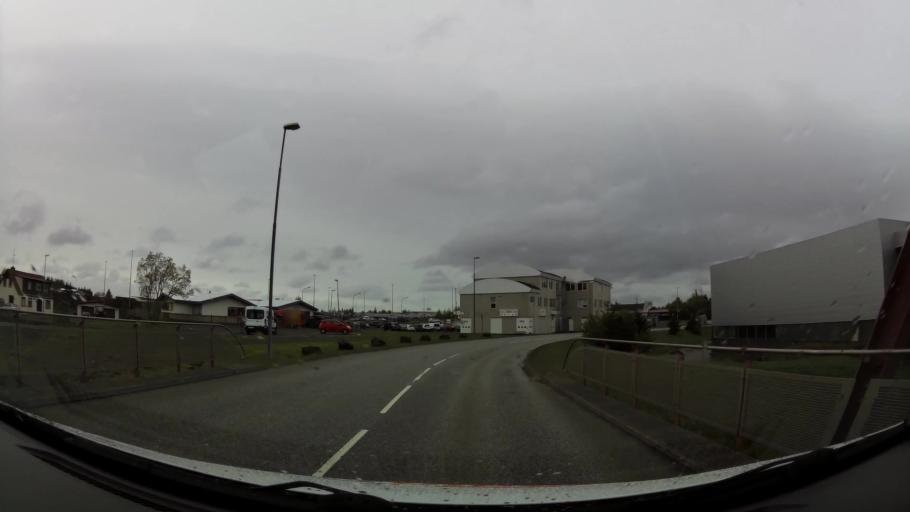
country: IS
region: Capital Region
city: Hafnarfjoerdur
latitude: 64.0659
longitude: -21.9354
